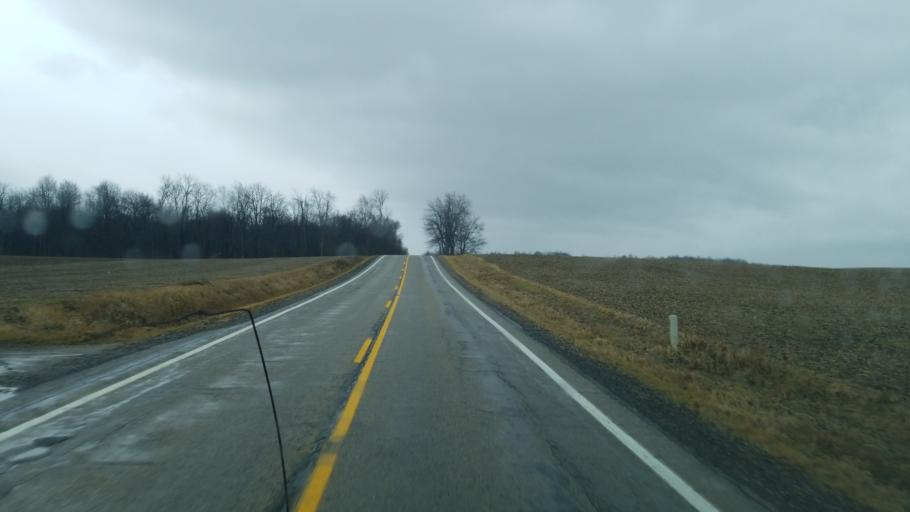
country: US
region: Ohio
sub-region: Crawford County
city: Bucyrus
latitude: 40.8700
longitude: -82.8550
